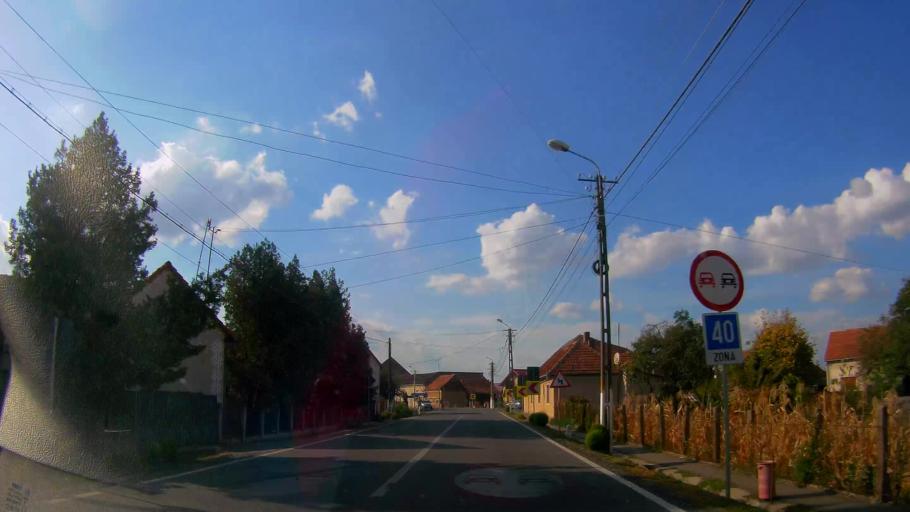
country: RO
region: Satu Mare
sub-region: Comuna Halmeu
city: Halmeu
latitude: 47.9751
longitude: 23.0281
